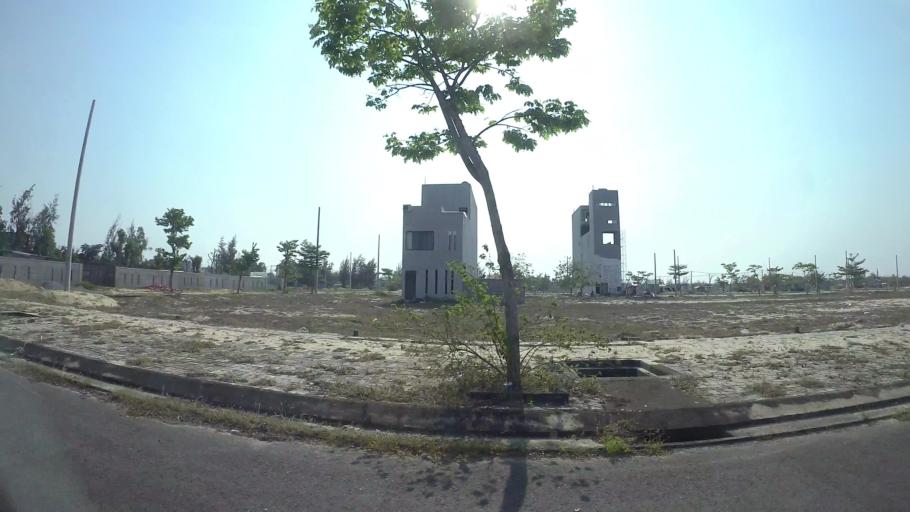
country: VN
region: Da Nang
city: Ngu Hanh Son
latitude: 15.9535
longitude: 108.2759
